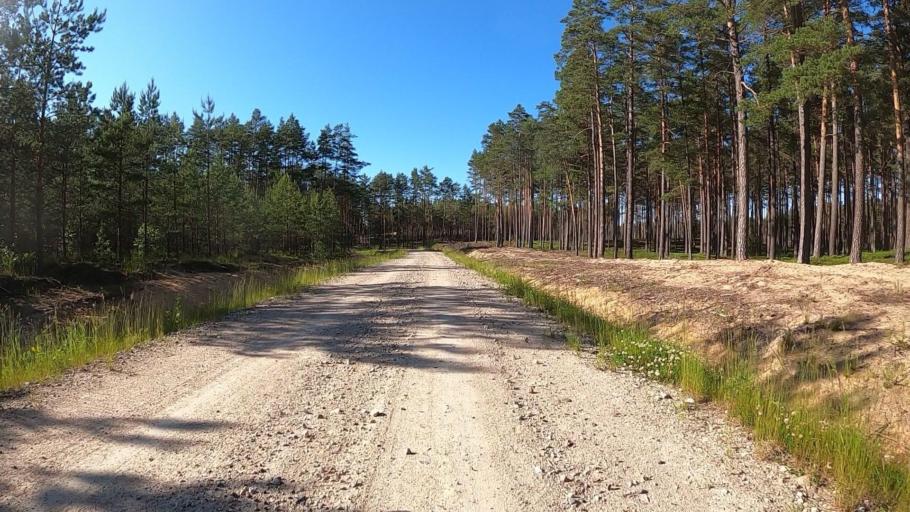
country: LV
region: Carnikava
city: Carnikava
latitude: 57.0979
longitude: 24.2416
